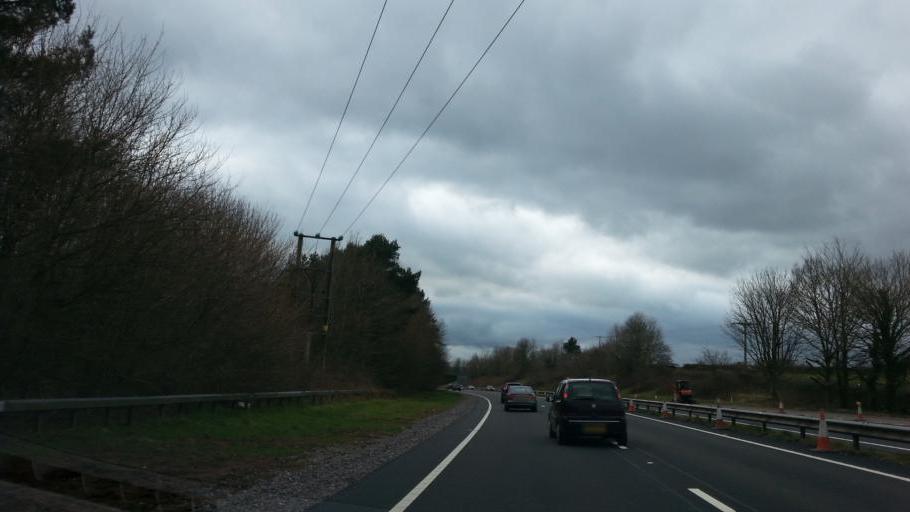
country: GB
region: England
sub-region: Devon
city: Tiverton
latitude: 50.9174
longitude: -3.4758
